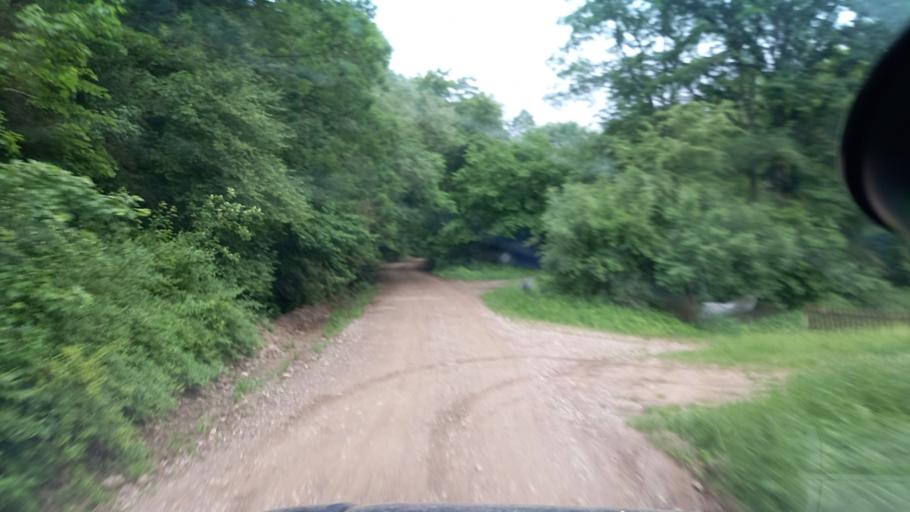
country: RU
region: Krasnodarskiy
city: Azovskaya
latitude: 44.6359
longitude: 38.6195
